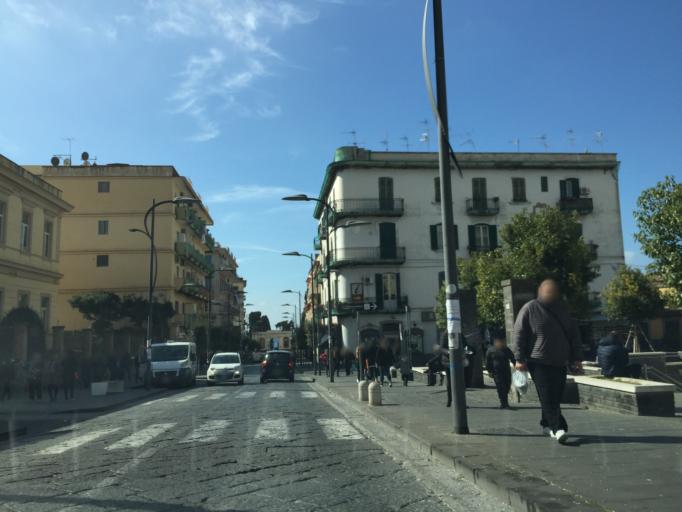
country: IT
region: Campania
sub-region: Provincia di Napoli
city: Ercolano
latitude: 40.8070
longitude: 14.3510
